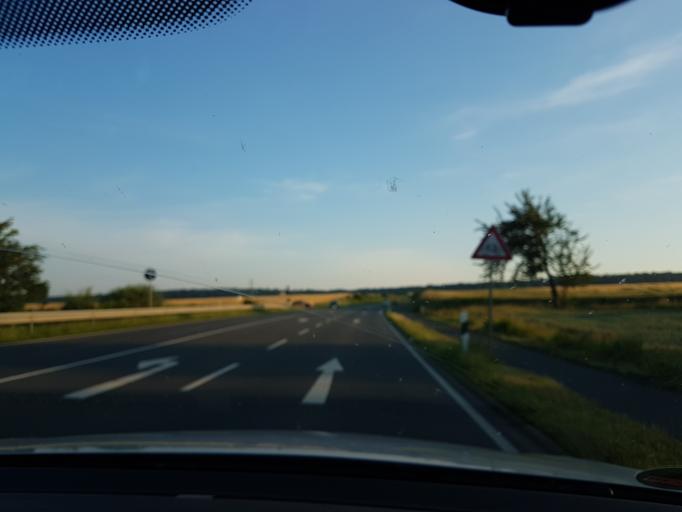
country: DE
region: Lower Saxony
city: Wolsdorf
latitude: 52.1947
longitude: 10.9689
